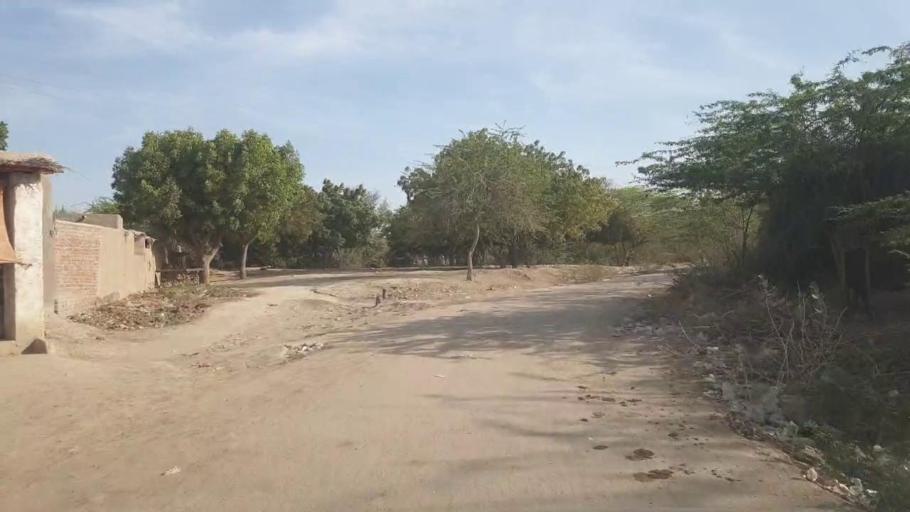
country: PK
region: Sindh
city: Nabisar
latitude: 25.0670
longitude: 69.6395
